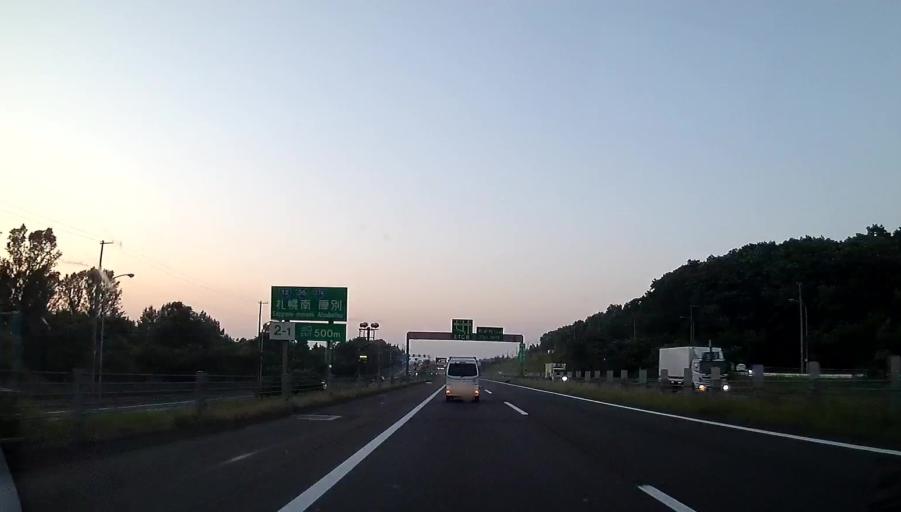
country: JP
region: Hokkaido
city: Kitahiroshima
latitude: 43.0047
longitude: 141.4670
